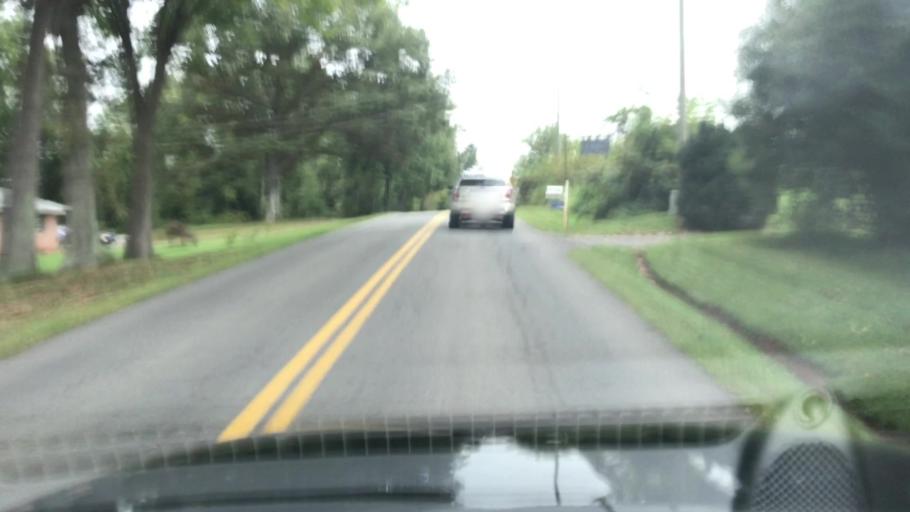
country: US
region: Virginia
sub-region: Fauquier County
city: New Baltimore
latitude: 38.7264
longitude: -77.6612
